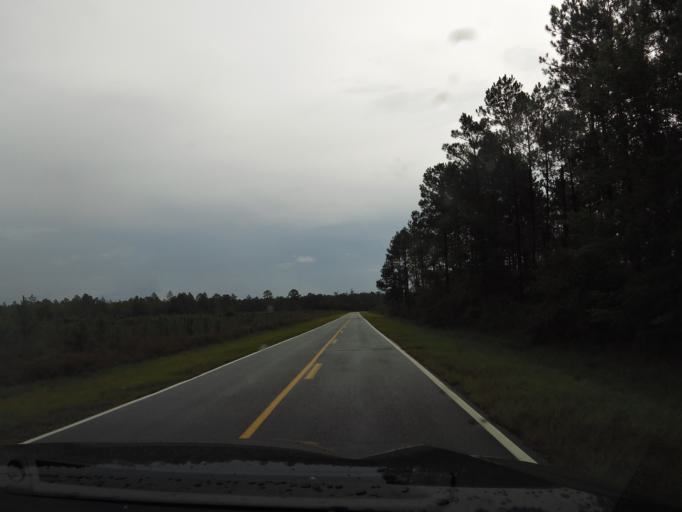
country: US
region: Georgia
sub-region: Wayne County
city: Jesup
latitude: 31.5468
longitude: -81.8662
